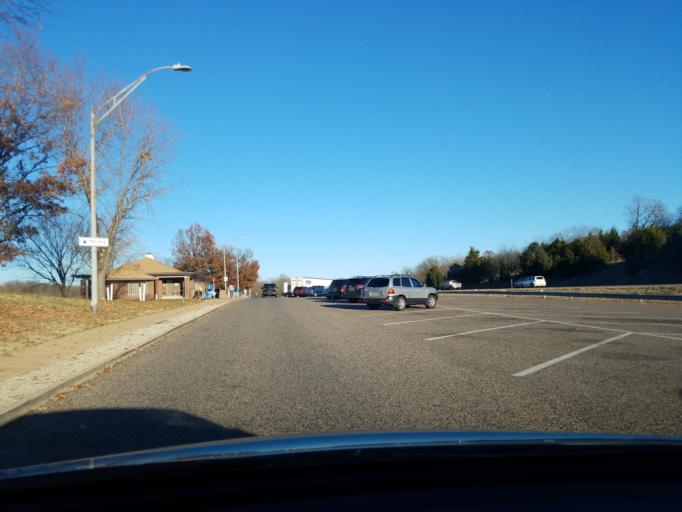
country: US
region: Missouri
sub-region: Franklin County
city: Saint Clair
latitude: 38.3152
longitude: -91.0490
